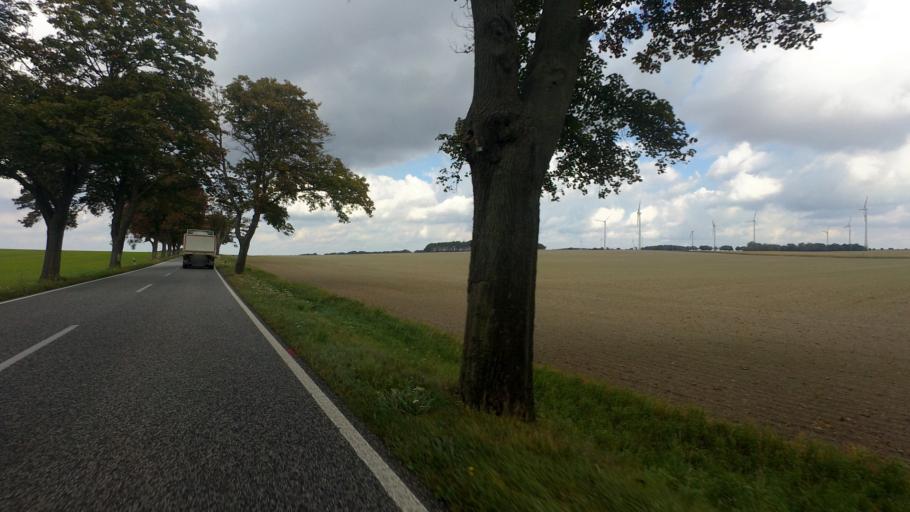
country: DE
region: Brandenburg
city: Juterbog
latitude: 51.9587
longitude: 13.1121
